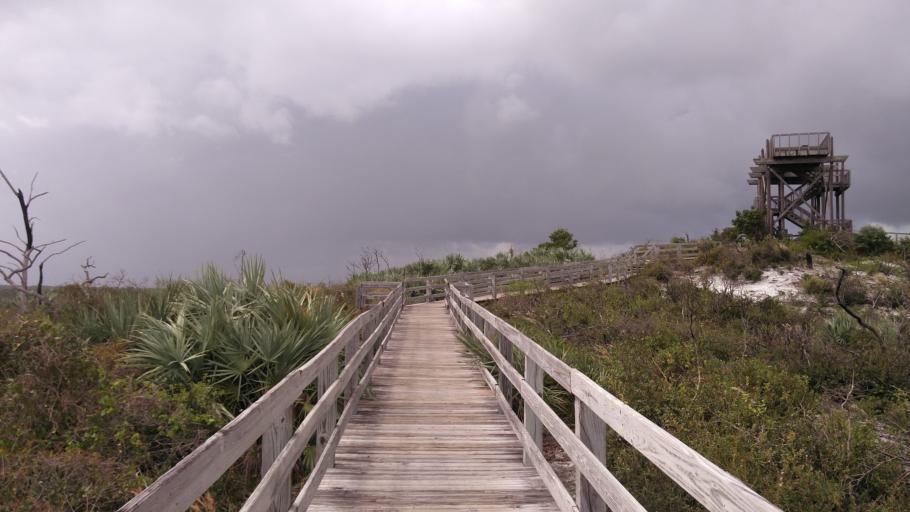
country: US
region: Florida
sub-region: Martin County
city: Hobe Sound
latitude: 27.0178
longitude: -80.1109
